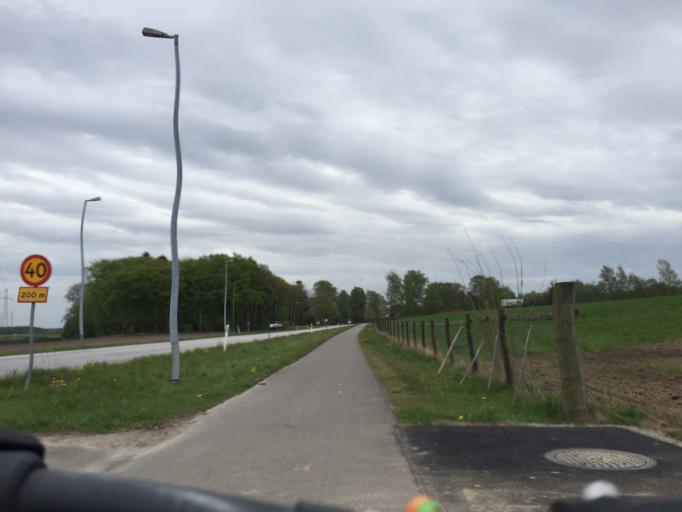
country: SE
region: Skane
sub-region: Lunds Kommun
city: Veberod
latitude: 55.6435
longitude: 13.4747
